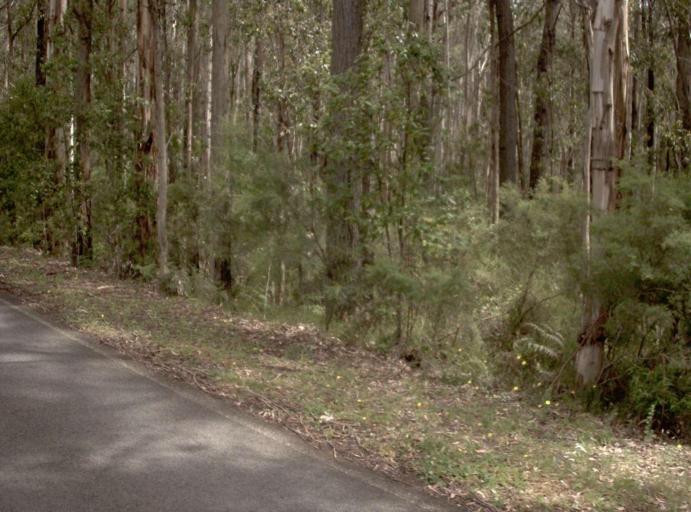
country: AU
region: Victoria
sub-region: Latrobe
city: Moe
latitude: -37.9805
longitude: 146.3974
